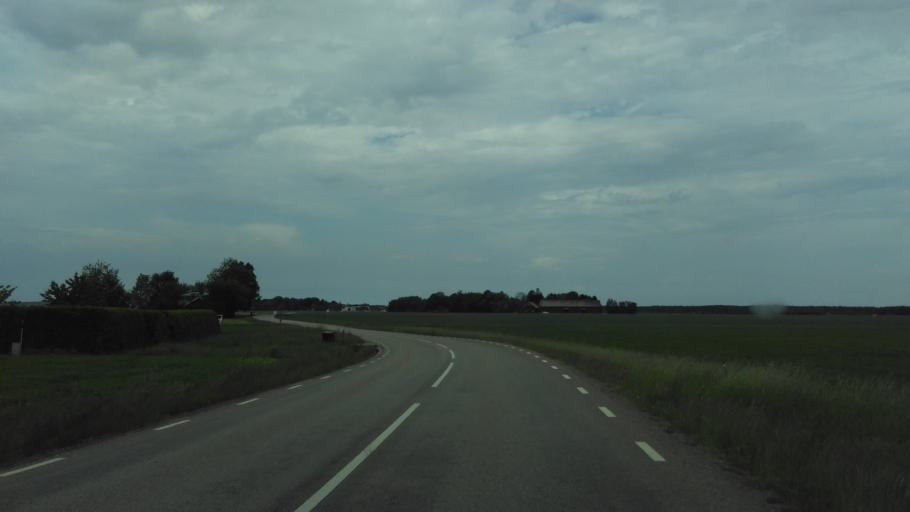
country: SE
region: Vaestra Goetaland
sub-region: Lidkopings Kommun
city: Lidkoping
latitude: 58.4502
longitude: 13.1606
